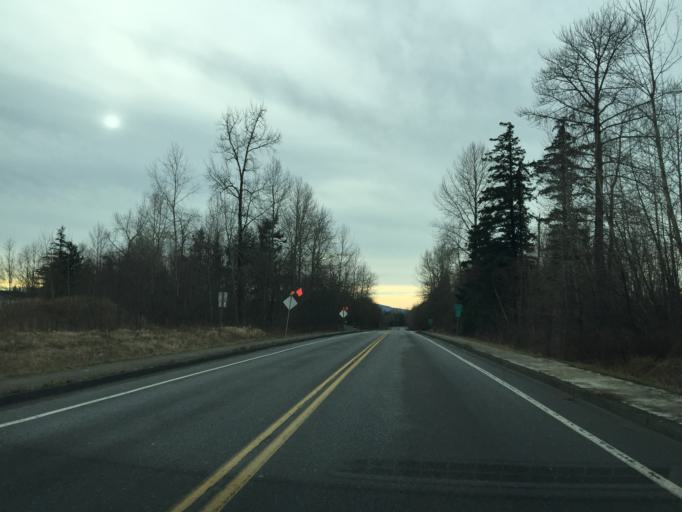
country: US
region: Washington
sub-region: Whatcom County
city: Marietta-Alderwood
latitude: 48.7852
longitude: -122.5265
